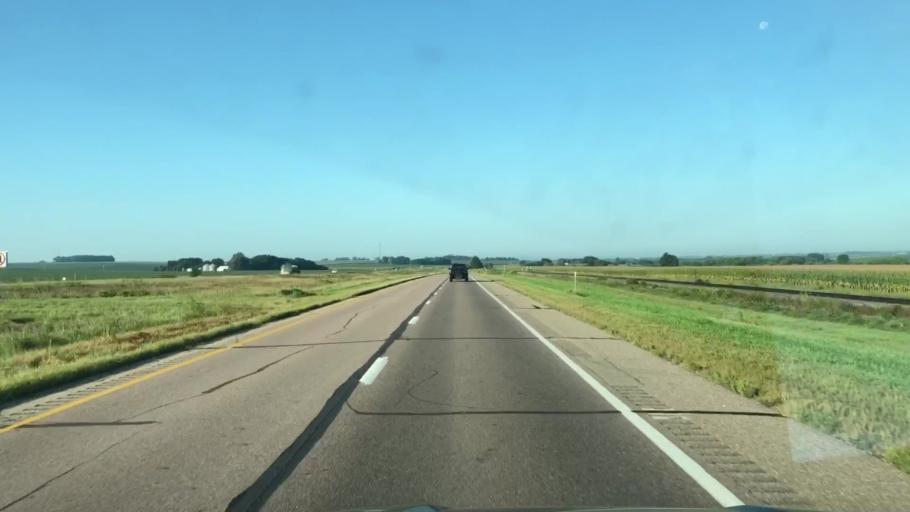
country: US
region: Iowa
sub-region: Sioux County
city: Alton
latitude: 43.0199
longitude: -95.9540
